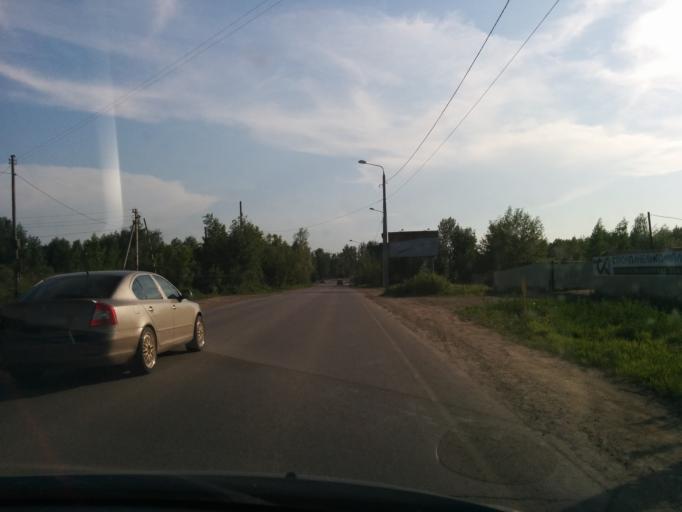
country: RU
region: Perm
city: Perm
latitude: 58.0375
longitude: 56.2597
